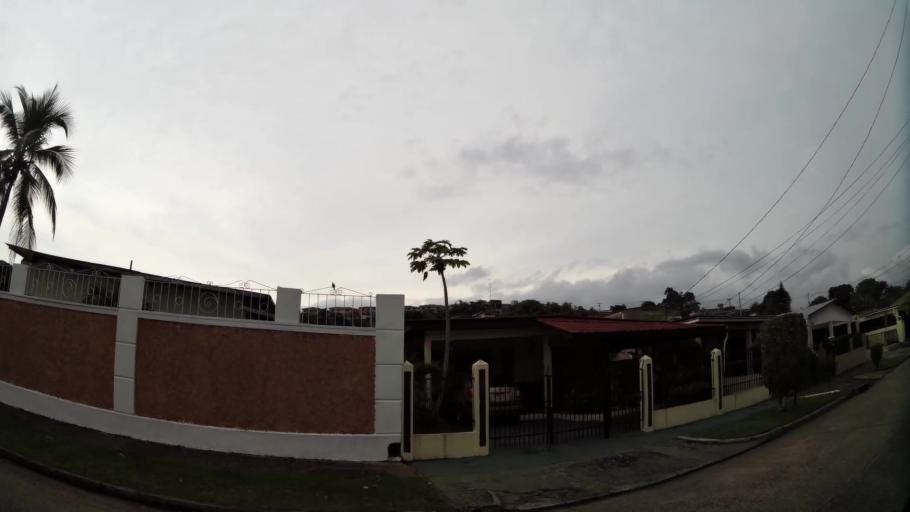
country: PA
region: Panama
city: Panama
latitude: 9.0182
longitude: -79.5277
